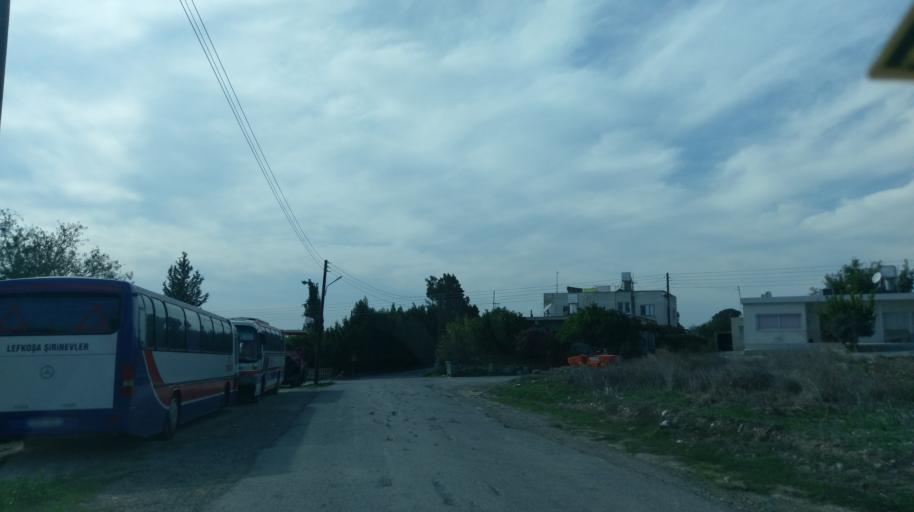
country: CY
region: Keryneia
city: Lapithos
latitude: 35.2754
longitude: 33.1713
